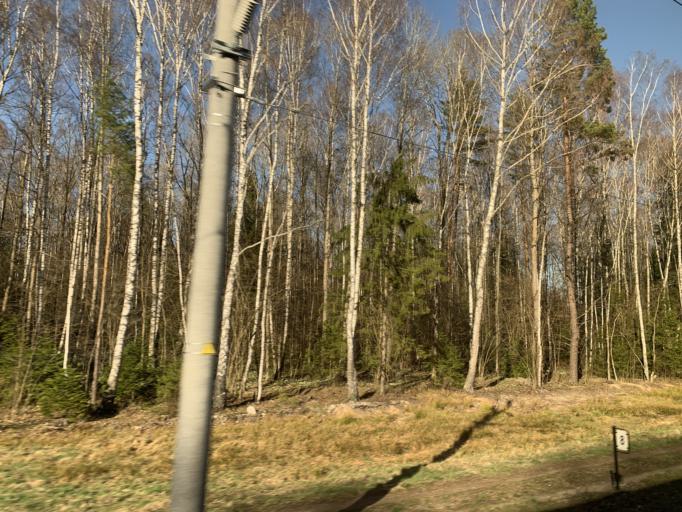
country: BY
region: Grodnenskaya
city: Smarhon'
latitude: 54.4887
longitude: 26.3050
